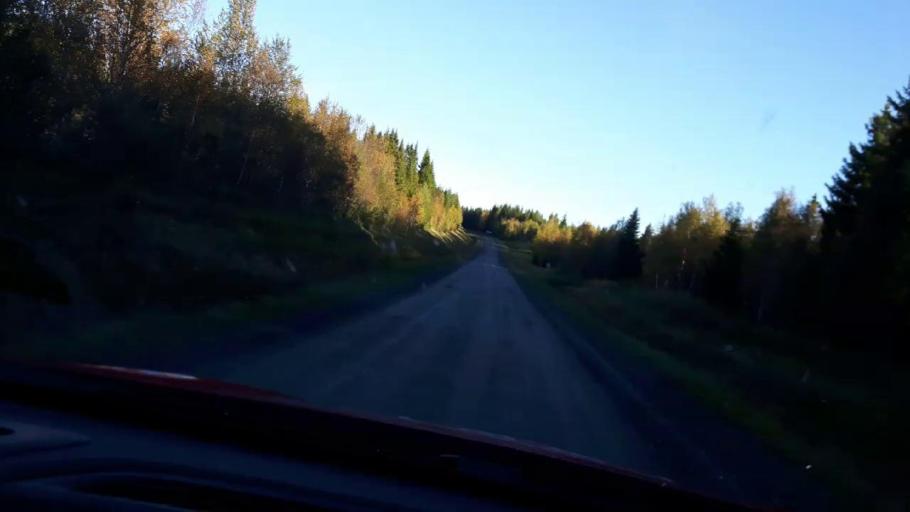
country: SE
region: Jaemtland
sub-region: OEstersunds Kommun
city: Lit
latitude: 63.5749
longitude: 14.8657
